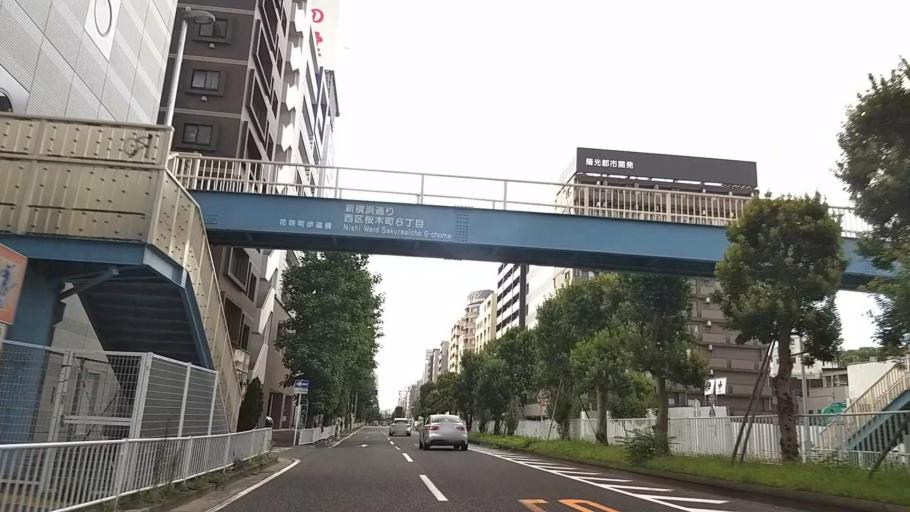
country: JP
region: Kanagawa
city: Yokohama
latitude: 35.4561
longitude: 139.6258
